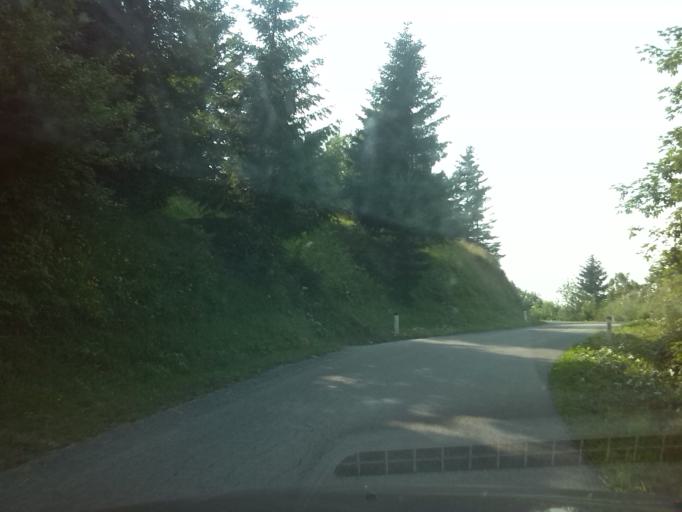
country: IT
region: Friuli Venezia Giulia
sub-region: Provincia di Udine
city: Cras
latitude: 46.1893
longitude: 13.6464
